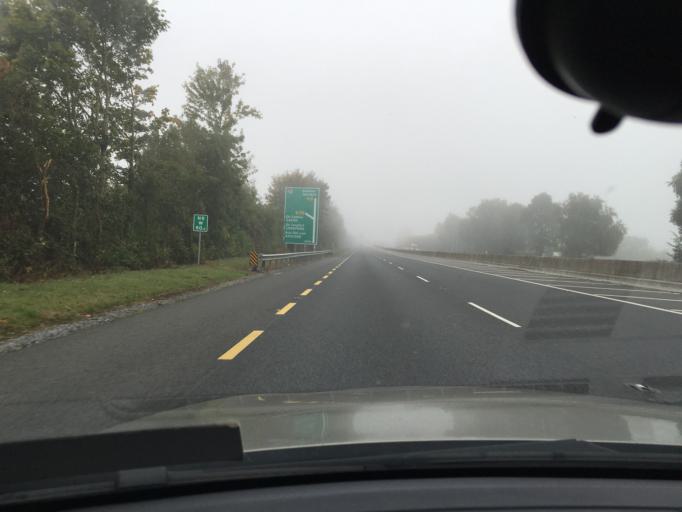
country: IE
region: Leinster
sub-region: An Iarmhi
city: Athlone
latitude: 53.4277
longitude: -7.9127
